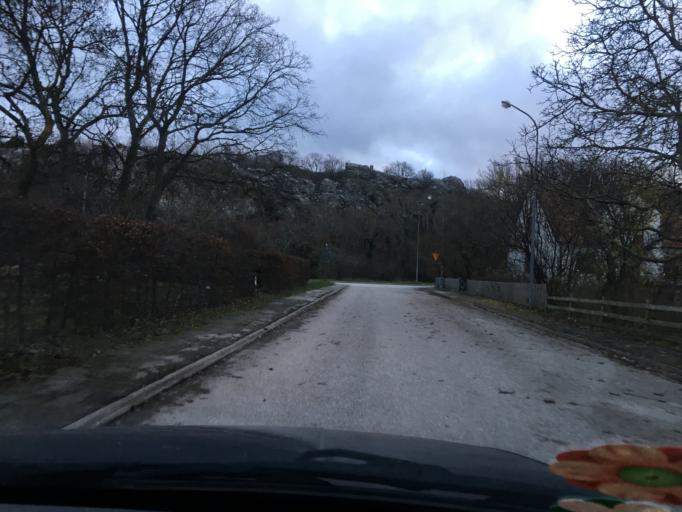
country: SE
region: Gotland
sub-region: Gotland
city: Visby
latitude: 57.6516
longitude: 18.3048
